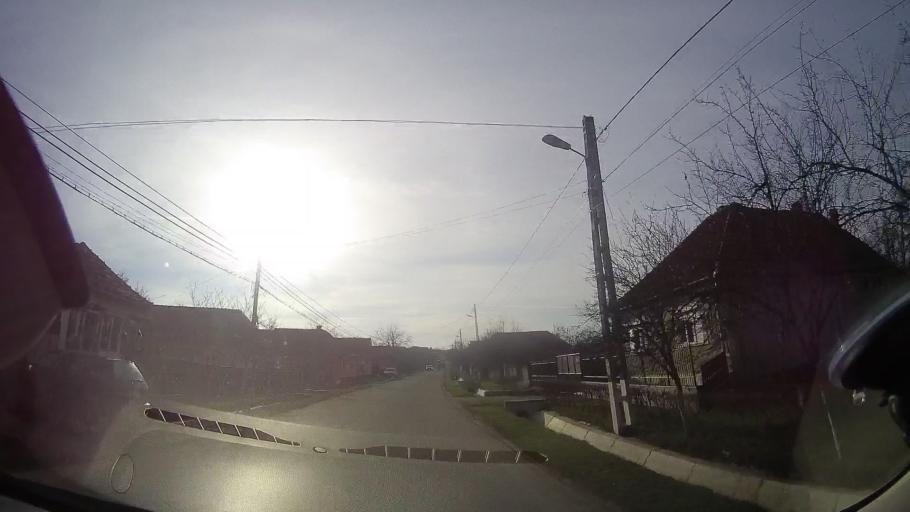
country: RO
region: Bihor
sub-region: Comuna Sarbi
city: Sarbi
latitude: 47.1970
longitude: 22.1238
